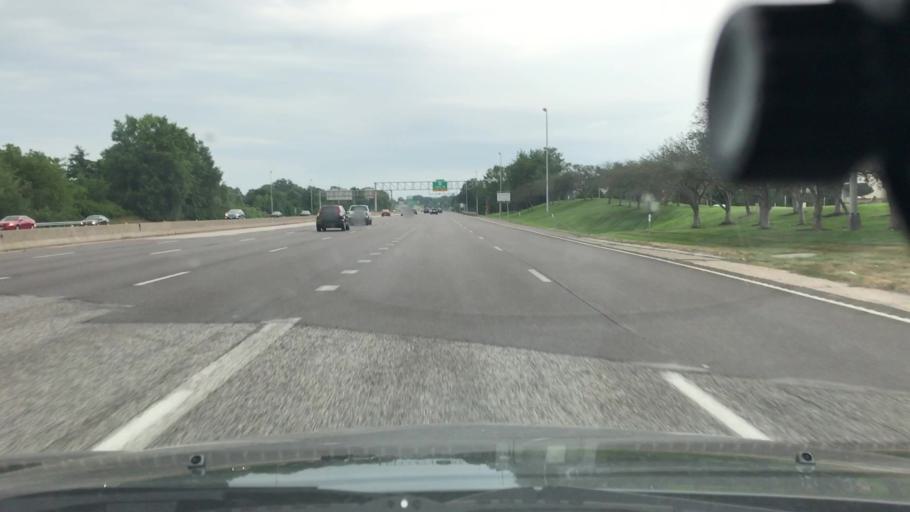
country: US
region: Missouri
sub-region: Saint Louis County
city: Creve Coeur
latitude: 38.6435
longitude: -90.4490
